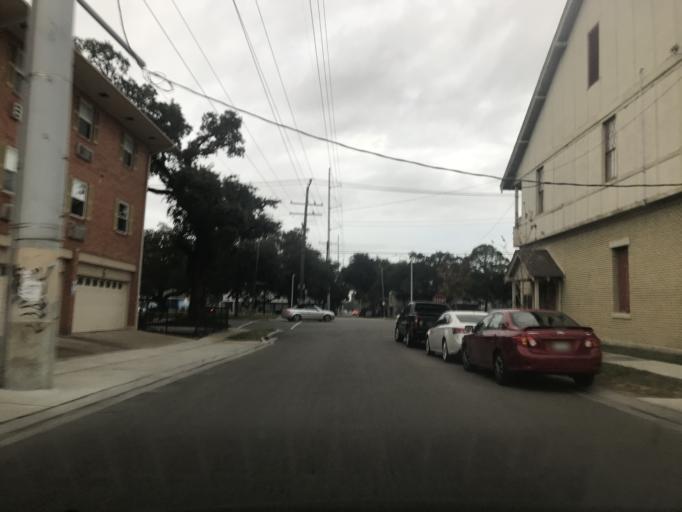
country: US
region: Louisiana
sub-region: Orleans Parish
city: New Orleans
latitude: 29.9662
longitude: -90.0966
